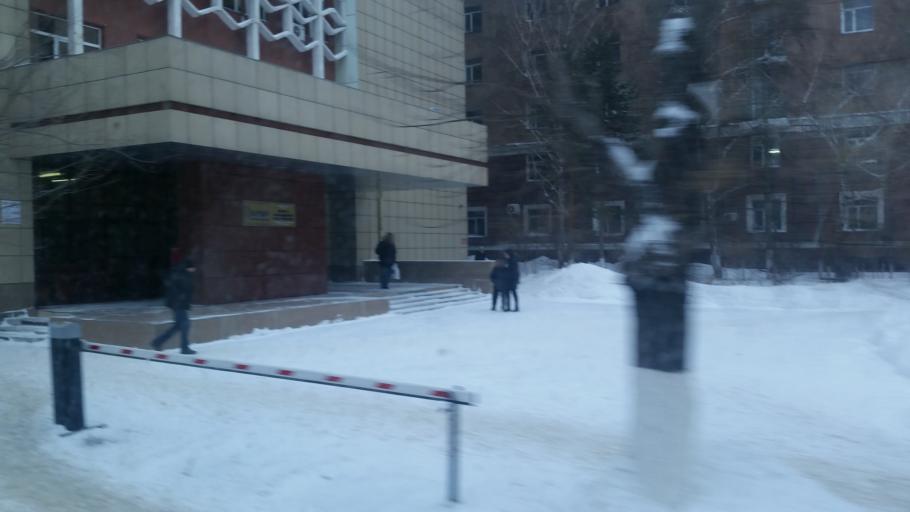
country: KZ
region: Qaraghandy
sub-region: Qaraghandy Qalasy
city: Karagandy
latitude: 49.8017
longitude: 73.0893
